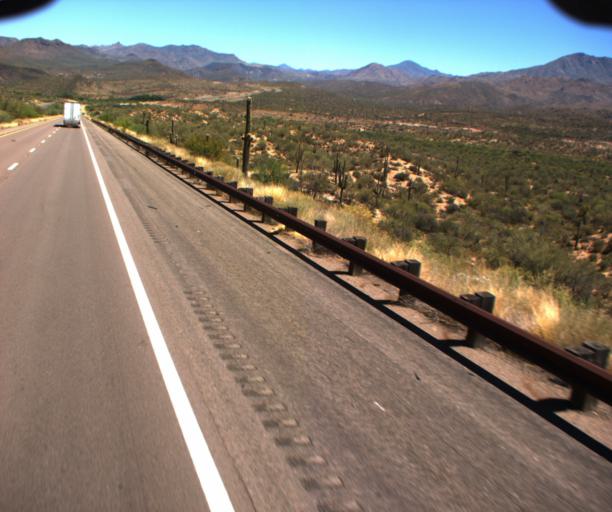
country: US
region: Arizona
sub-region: Maricopa County
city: Rio Verde
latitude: 33.7153
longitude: -111.5103
